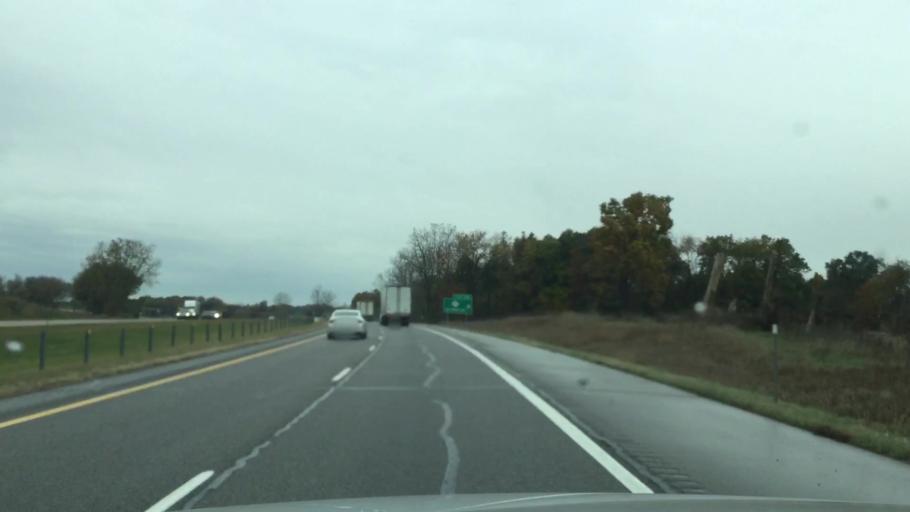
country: US
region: Michigan
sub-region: Calhoun County
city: Albion
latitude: 42.2830
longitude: -84.7940
